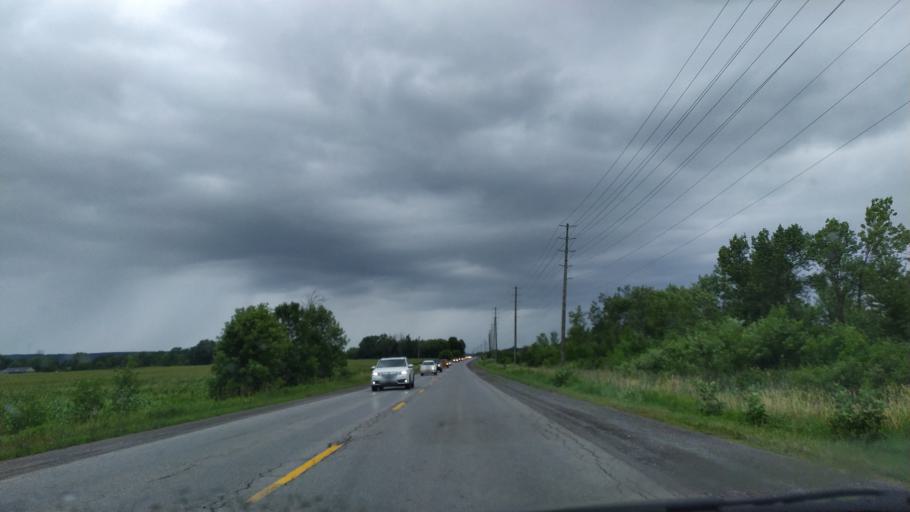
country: CA
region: Ontario
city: Quinte West
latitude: 44.0849
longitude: -77.6093
